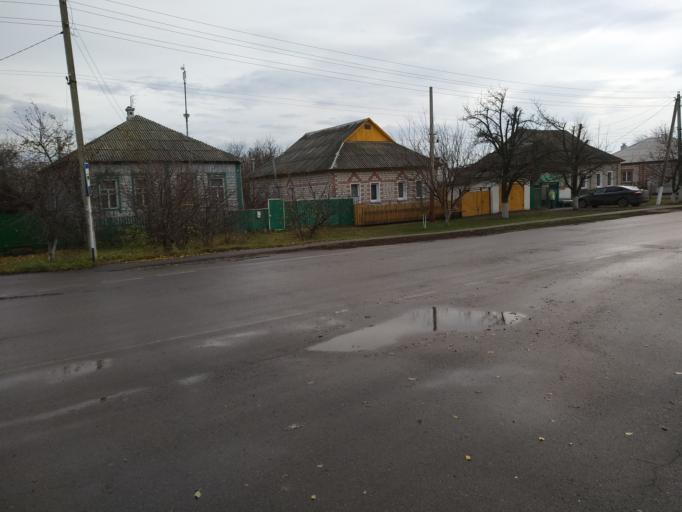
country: RU
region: Voronezj
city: Liski
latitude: 51.0581
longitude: 39.4905
